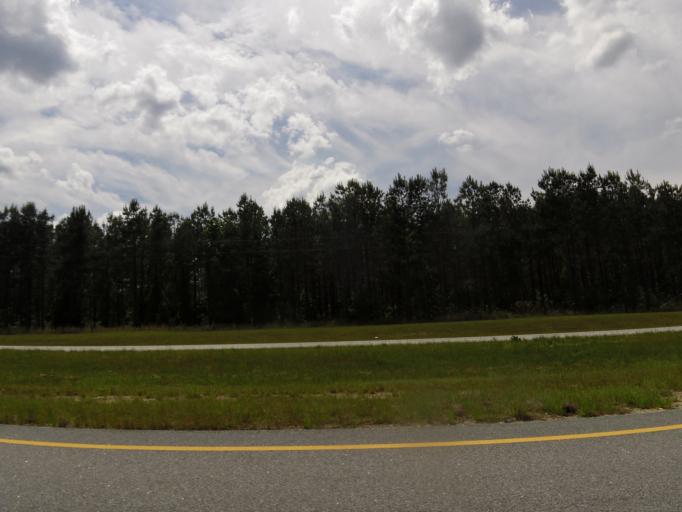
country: US
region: Georgia
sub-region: Jefferson County
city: Wadley
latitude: 32.7912
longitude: -82.3964
